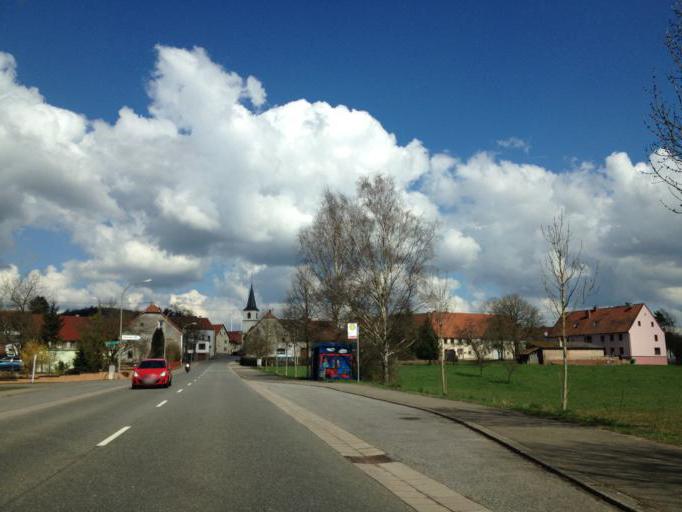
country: DE
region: Rheinland-Pfalz
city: Breitenbach
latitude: 49.4487
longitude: 7.2314
